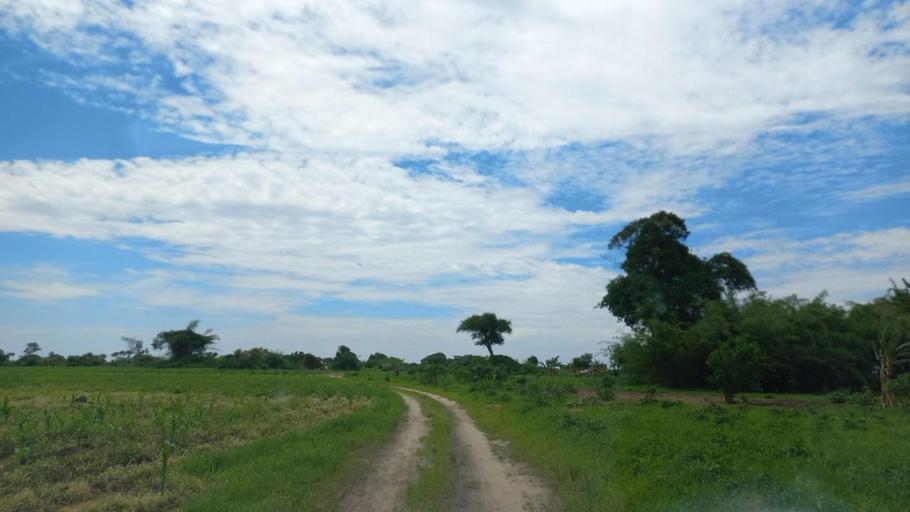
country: ZM
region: Copperbelt
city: Kitwe
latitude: -12.7953
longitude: 28.4013
